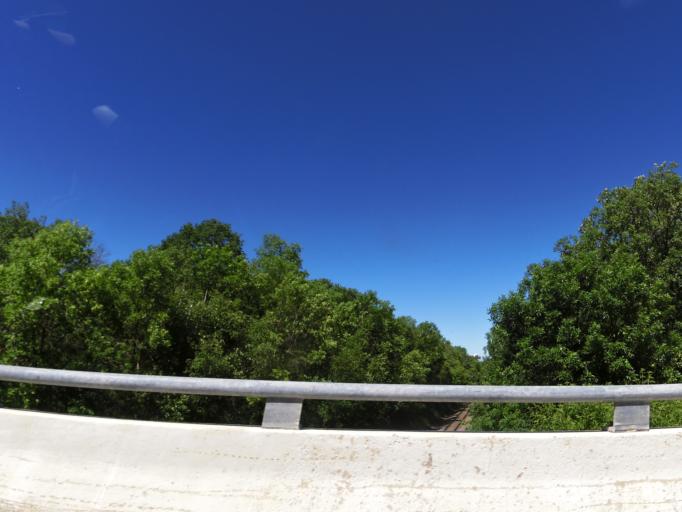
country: US
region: Minnesota
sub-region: Polk County
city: Fosston
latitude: 47.6600
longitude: -95.9833
